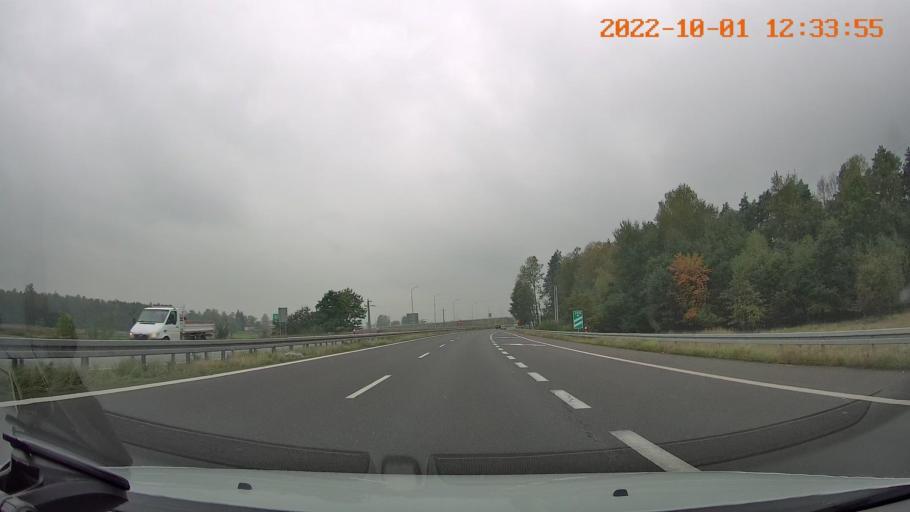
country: PL
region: Silesian Voivodeship
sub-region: Powiat bierunsko-ledzinski
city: Ledziny
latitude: 50.1445
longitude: 19.1031
